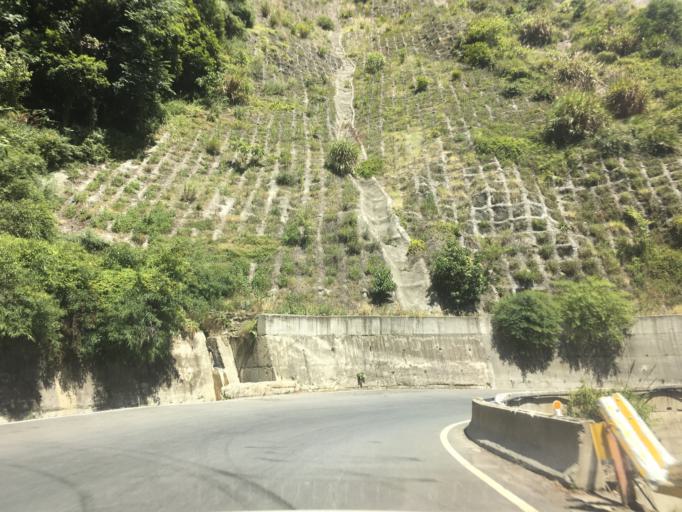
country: TW
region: Taiwan
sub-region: Nantou
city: Puli
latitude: 24.2359
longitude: 121.2532
